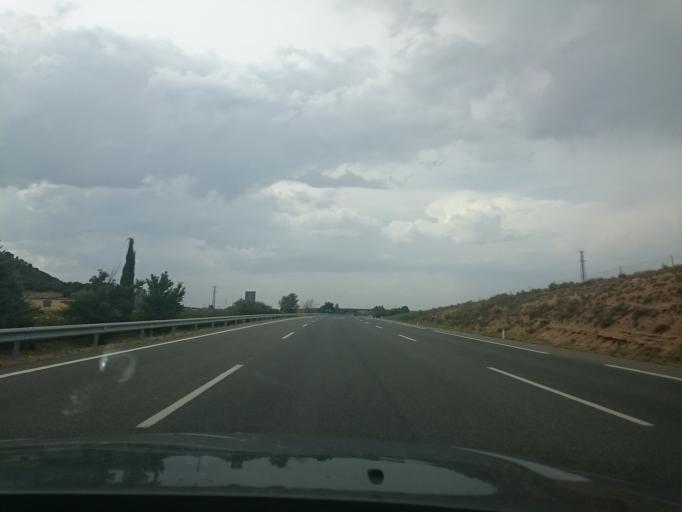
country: ES
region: Navarre
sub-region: Provincia de Navarra
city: Corella
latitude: 42.0869
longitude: -1.7147
